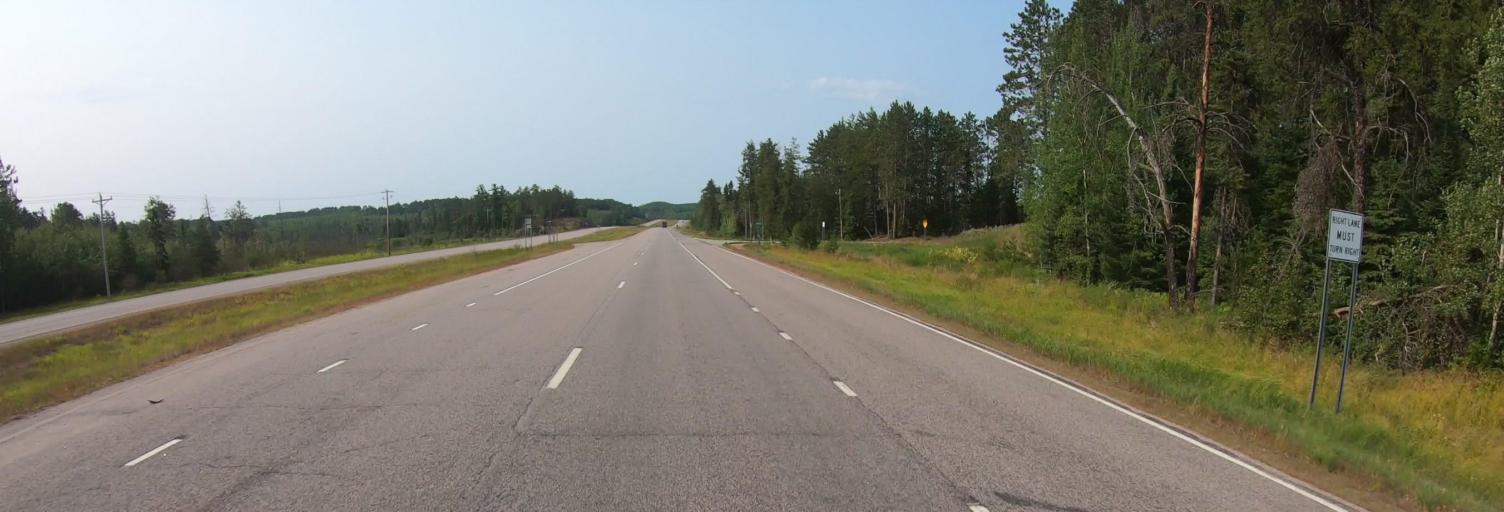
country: US
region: Minnesota
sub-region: Saint Louis County
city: Mountain Iron
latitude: 47.7001
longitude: -92.6453
